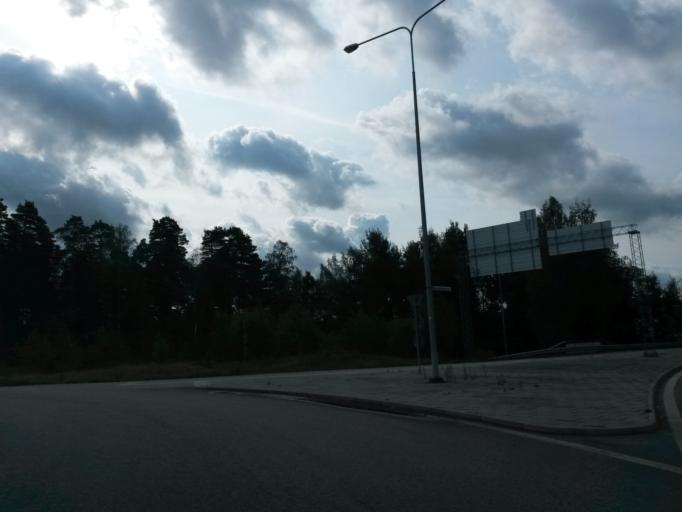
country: SE
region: Kronoberg
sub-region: Vaxjo Kommun
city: Vaexjoe
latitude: 56.8997
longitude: 14.8236
